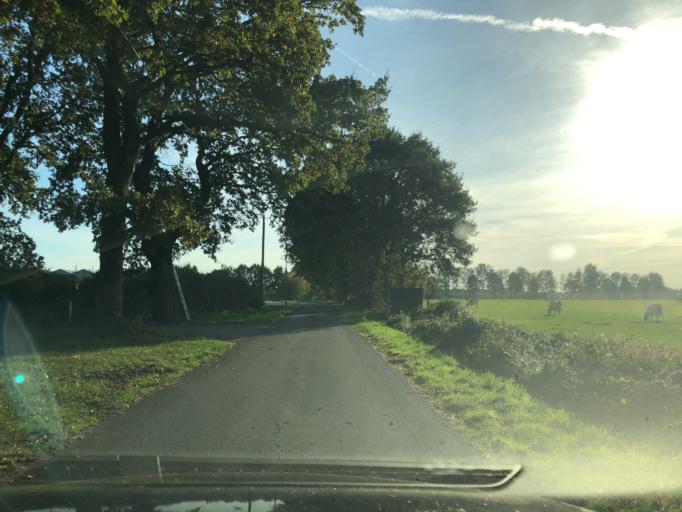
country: DE
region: Lower Saxony
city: Neulehe
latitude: 53.0383
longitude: 7.3735
